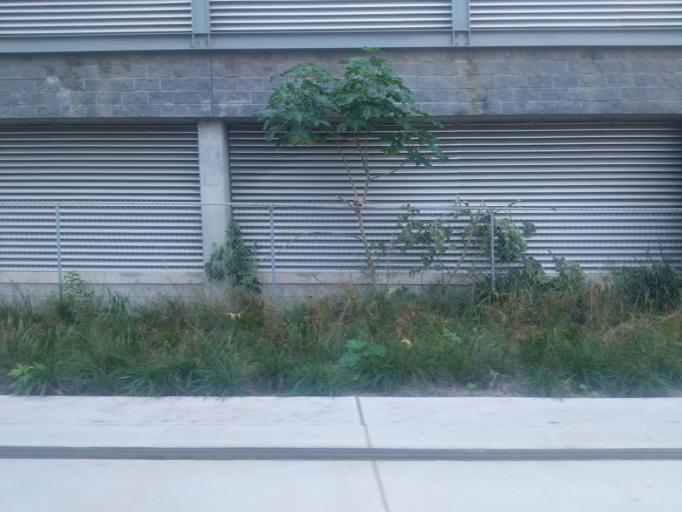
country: AU
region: New South Wales
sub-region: Newcastle
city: Cooks Hill
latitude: -32.9264
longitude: 151.7654
